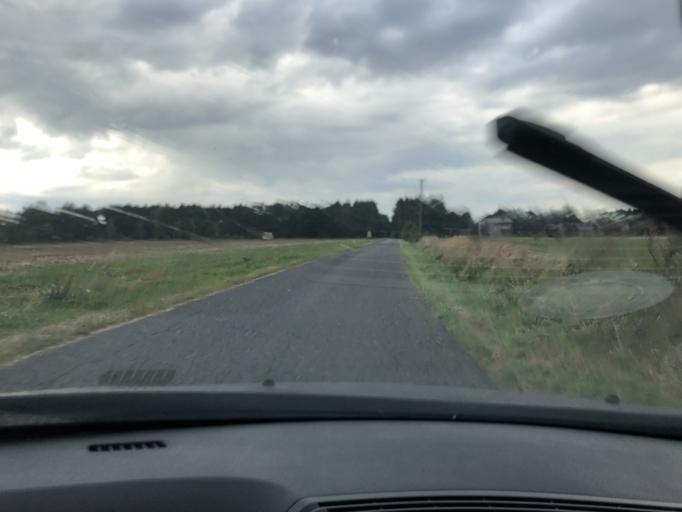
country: PL
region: Lodz Voivodeship
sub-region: Powiat wieruszowski
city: Czastary
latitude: 51.2414
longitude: 18.3008
